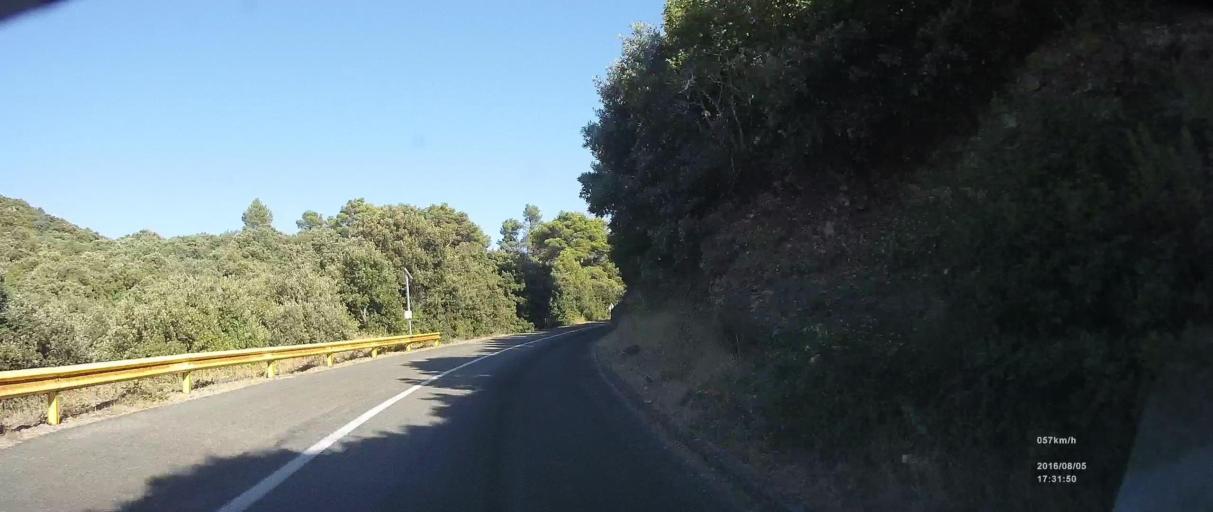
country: HR
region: Dubrovacko-Neretvanska
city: Blato
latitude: 42.7722
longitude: 17.4242
